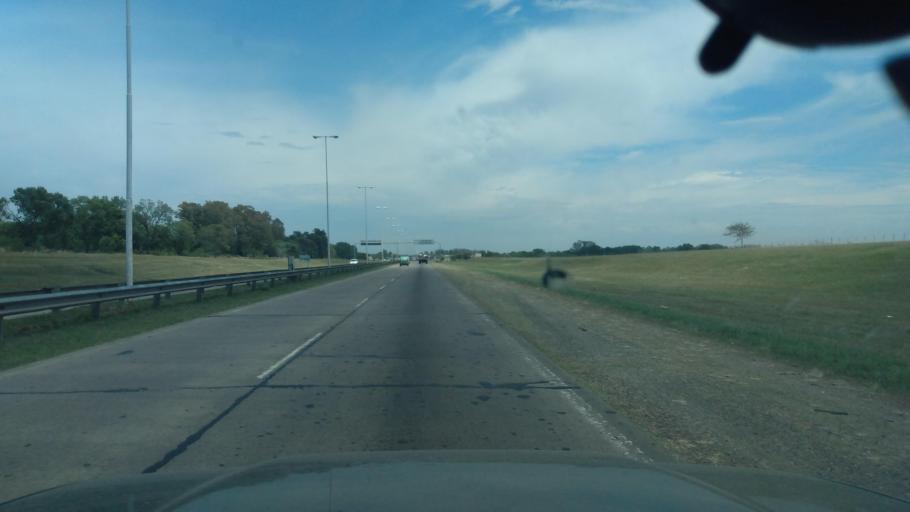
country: AR
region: Buenos Aires
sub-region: Partido de Lujan
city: Lujan
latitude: -34.5667
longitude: -59.0691
